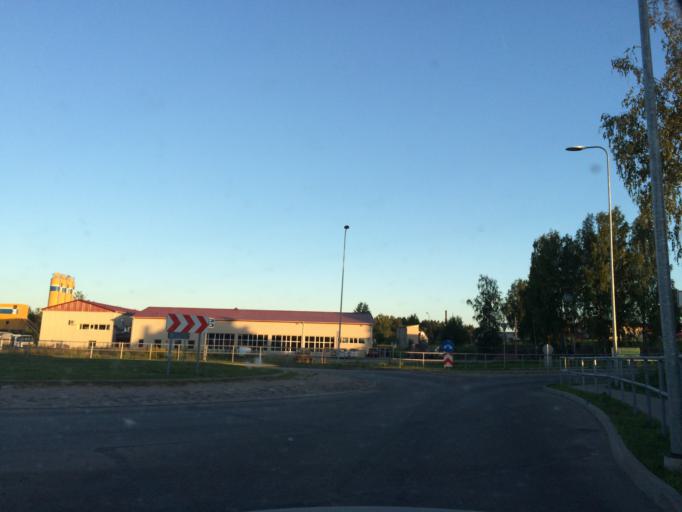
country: LV
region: Rezekne
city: Rezekne
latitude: 56.5129
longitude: 27.3578
